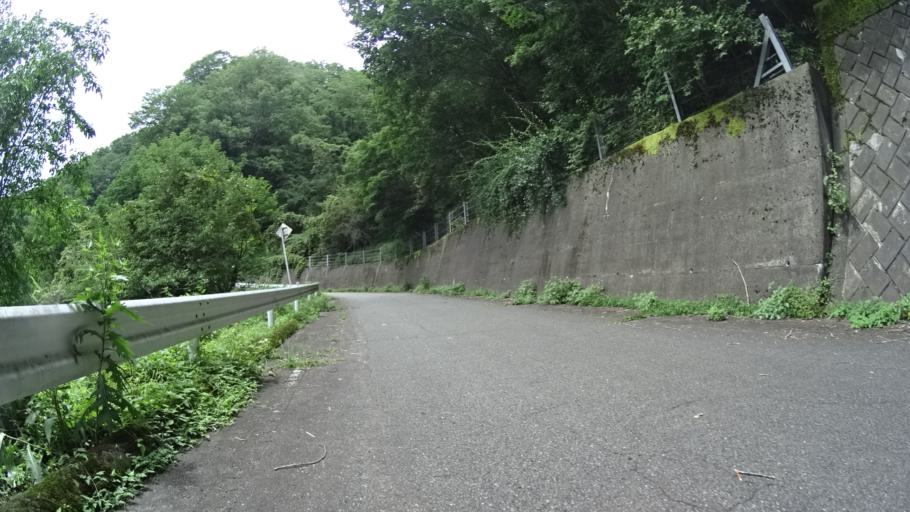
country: JP
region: Nagano
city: Saku
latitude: 36.0661
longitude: 138.6444
